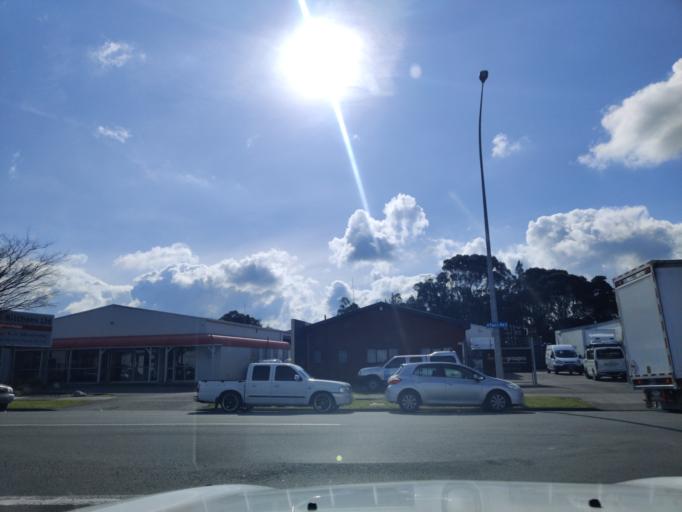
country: NZ
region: Manawatu-Wanganui
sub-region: Palmerston North City
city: Palmerston North
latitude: -40.3384
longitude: 175.6011
